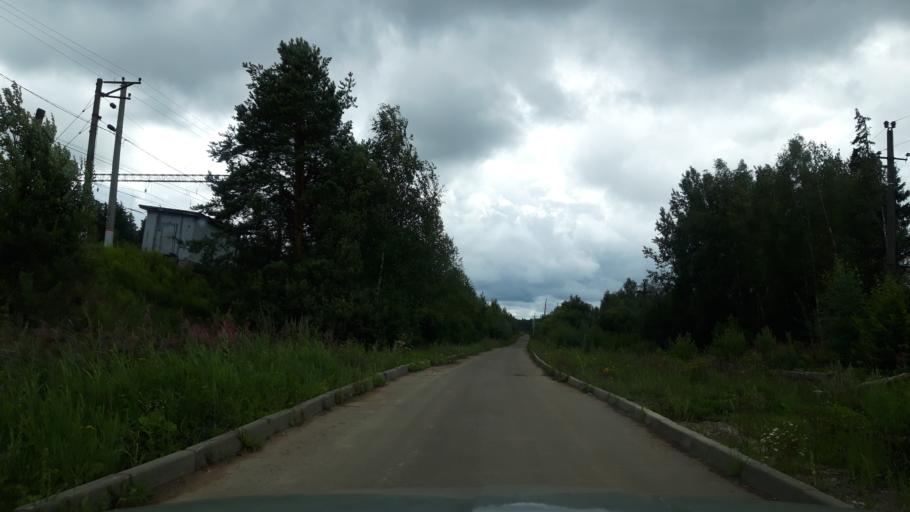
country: RU
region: Moskovskaya
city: Povarovo
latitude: 56.0438
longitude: 37.0548
